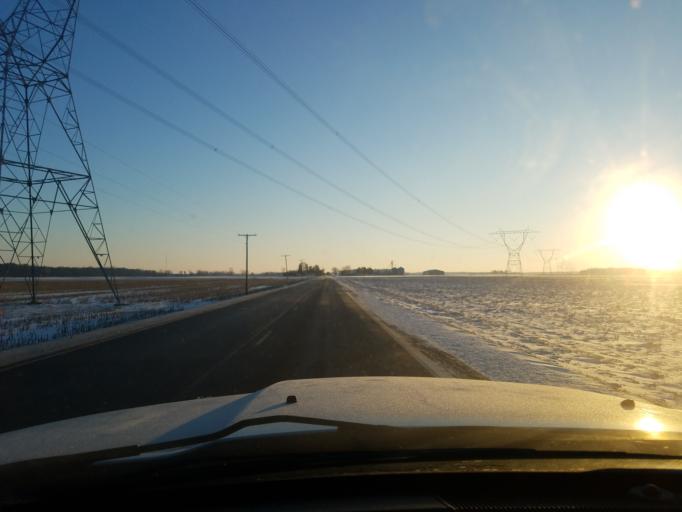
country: US
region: Indiana
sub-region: Marshall County
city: Bremen
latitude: 41.4499
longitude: -86.2302
